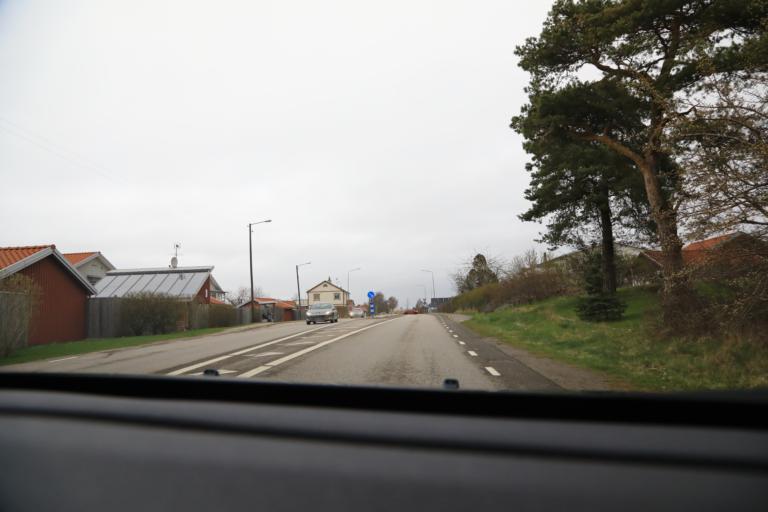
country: SE
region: Halland
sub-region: Kungsbacka Kommun
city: Frillesas
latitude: 57.3158
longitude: 12.1771
